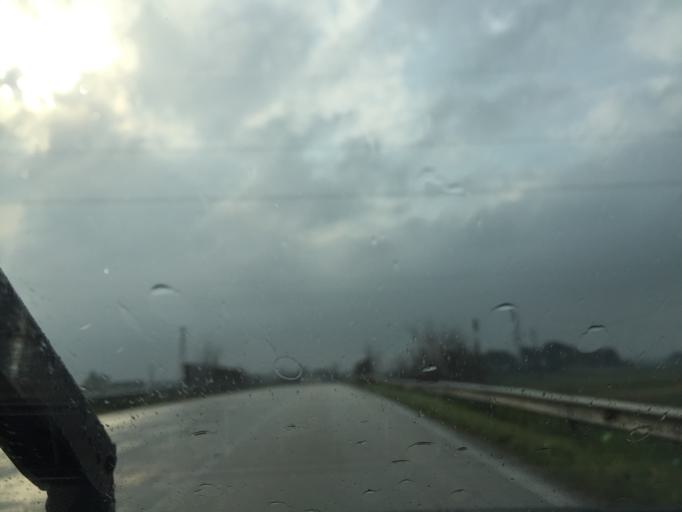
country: IT
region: Apulia
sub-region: Provincia di Foggia
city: Foggia
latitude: 41.4933
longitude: 15.5217
